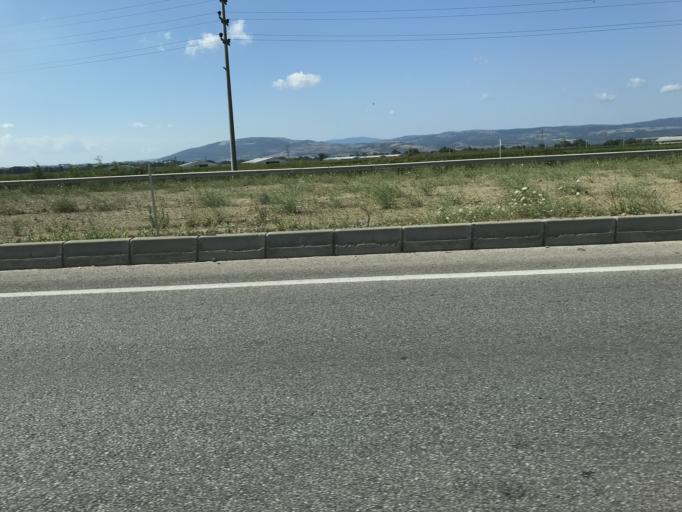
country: TR
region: Bursa
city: Karacabey
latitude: 40.1967
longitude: 28.4173
